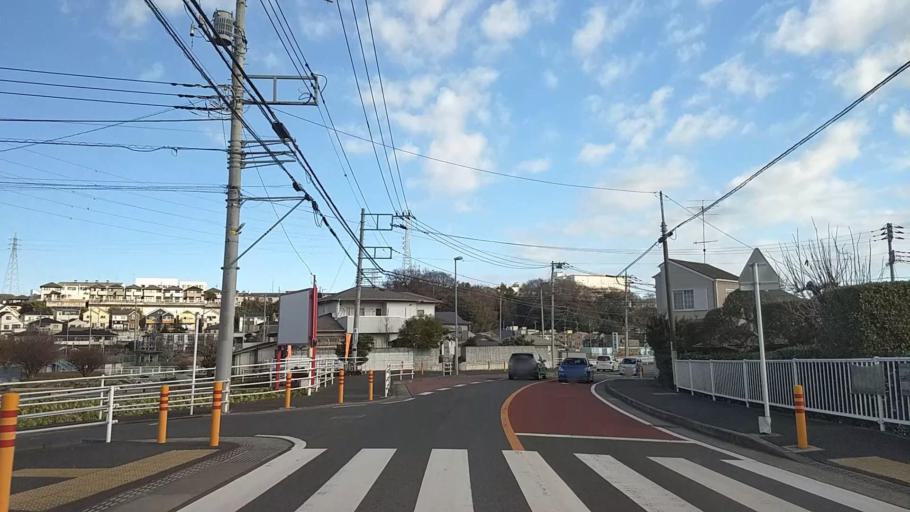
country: JP
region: Kanagawa
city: Atsugi
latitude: 35.4397
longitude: 139.3434
